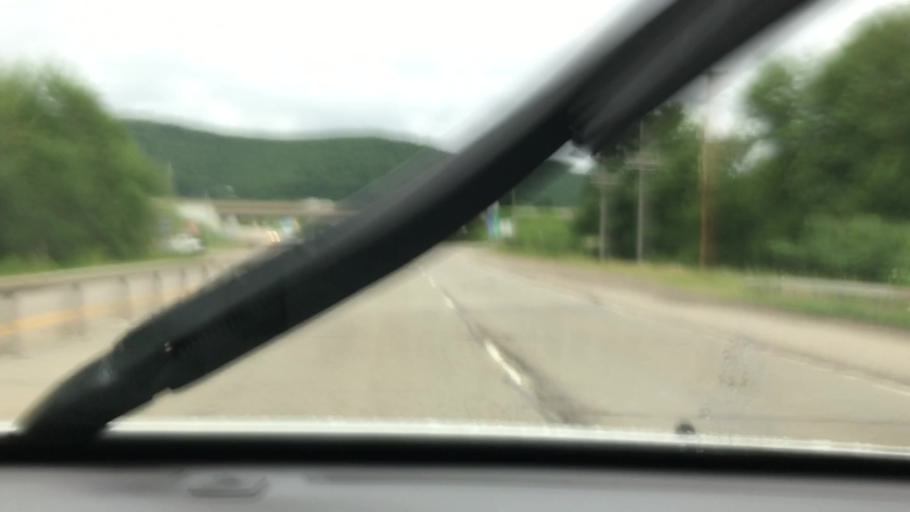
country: US
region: New York
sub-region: Cattaraugus County
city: Salamanca
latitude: 42.0867
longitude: -78.6318
